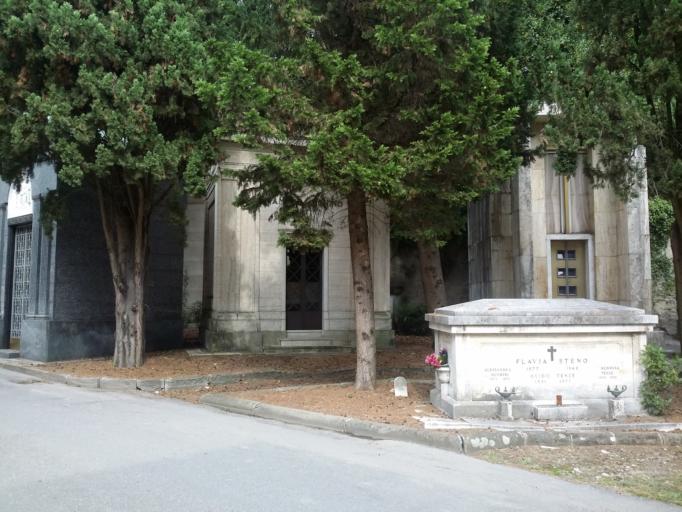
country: IT
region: Liguria
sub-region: Provincia di Genova
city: Genoa
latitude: 44.4293
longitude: 8.9481
